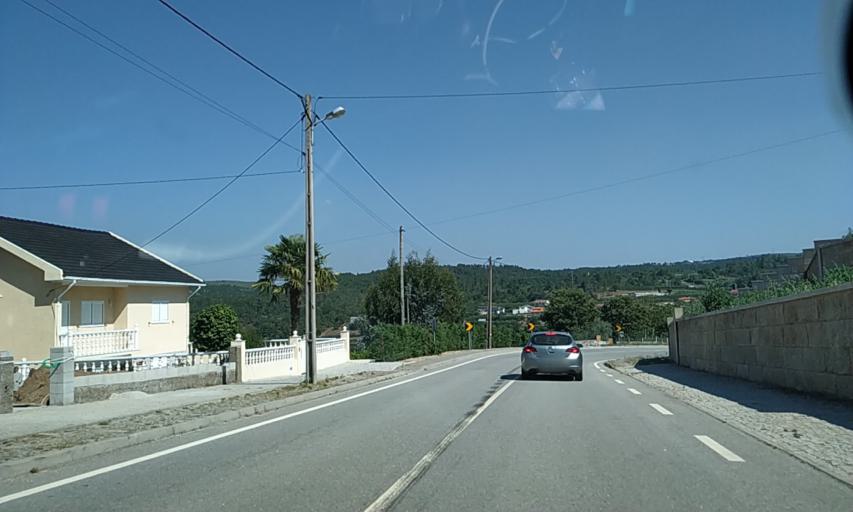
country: PT
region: Viseu
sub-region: Tarouca
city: Tarouca
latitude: 41.0256
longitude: -7.7118
